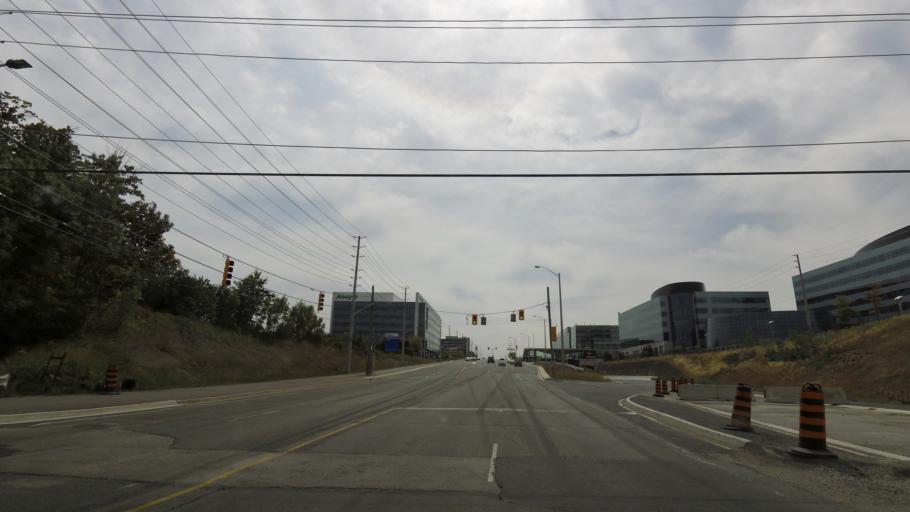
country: CA
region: Ontario
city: Etobicoke
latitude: 43.6462
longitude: -79.6092
